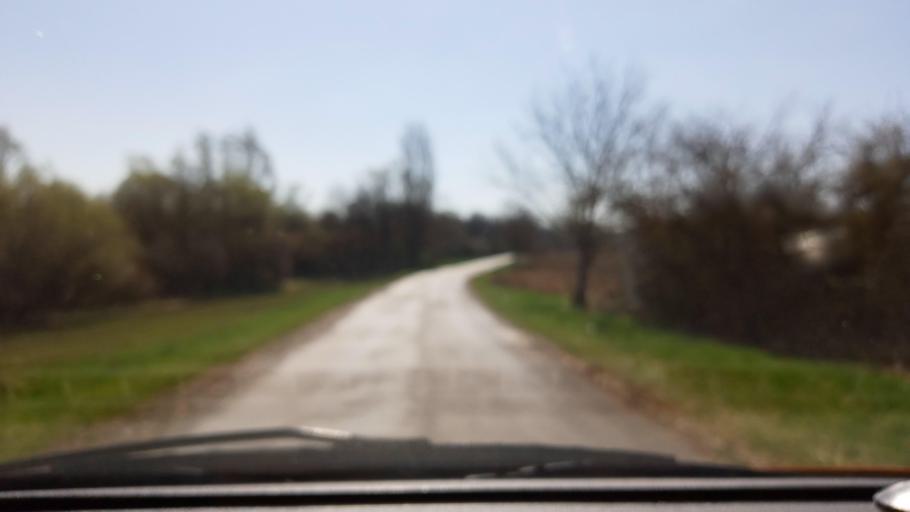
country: HU
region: Baranya
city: Kozarmisleny
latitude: 46.0717
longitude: 18.3635
